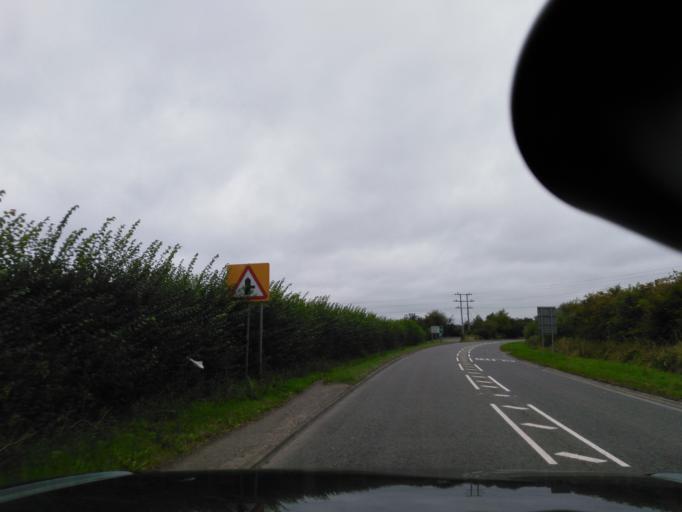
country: GB
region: England
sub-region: Wiltshire
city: Westbury
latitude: 51.2739
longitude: -2.1788
